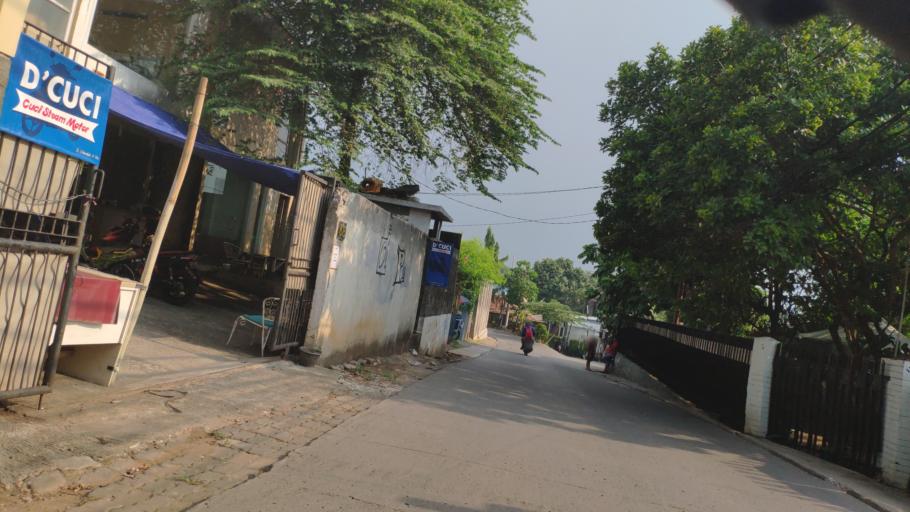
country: ID
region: Banten
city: South Tangerang
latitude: -6.2856
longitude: 106.7997
